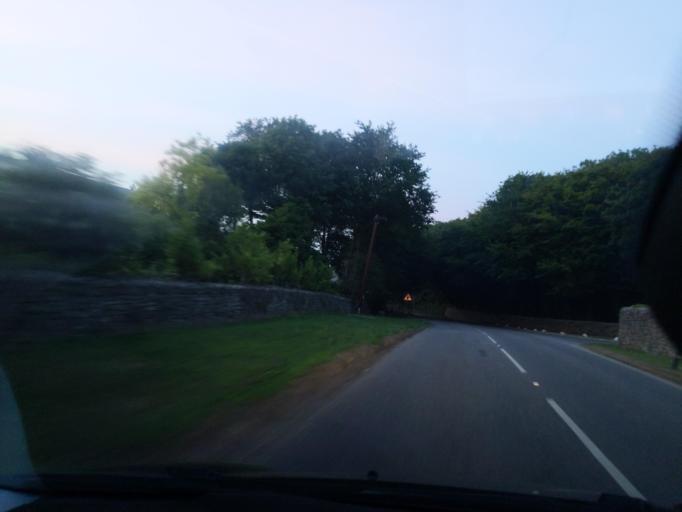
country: GB
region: England
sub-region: Cornwall
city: Camborne
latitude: 50.1981
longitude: -5.3054
